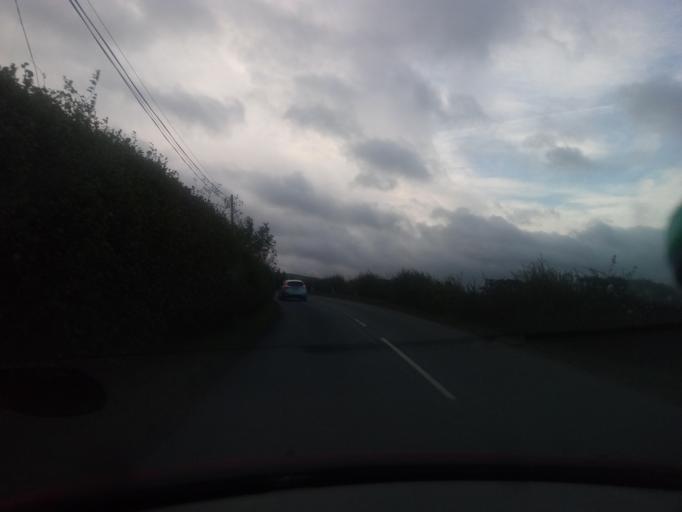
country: GB
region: Scotland
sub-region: The Scottish Borders
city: Jedburgh
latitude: 55.3901
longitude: -2.6461
